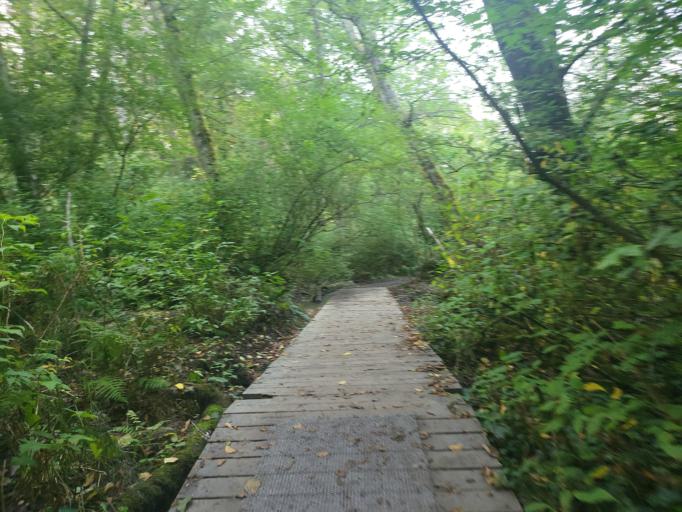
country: US
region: Washington
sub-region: Pierce County
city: Tacoma
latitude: 47.3165
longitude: -122.4143
